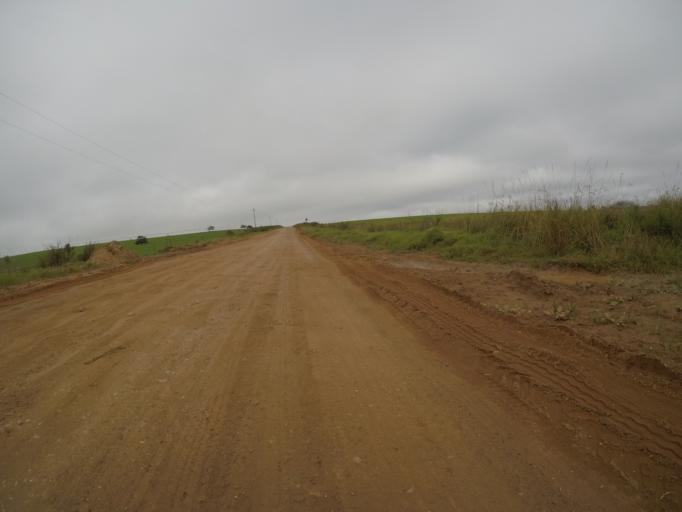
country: ZA
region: Eastern Cape
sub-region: Cacadu District Municipality
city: Kareedouw
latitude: -34.0191
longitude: 24.2393
